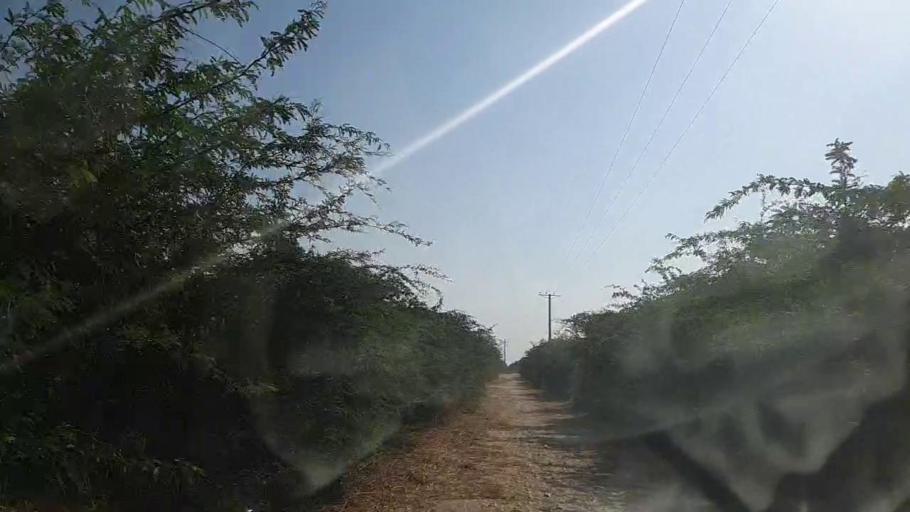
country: PK
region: Sindh
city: Mirpur Batoro
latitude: 24.6523
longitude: 68.1783
